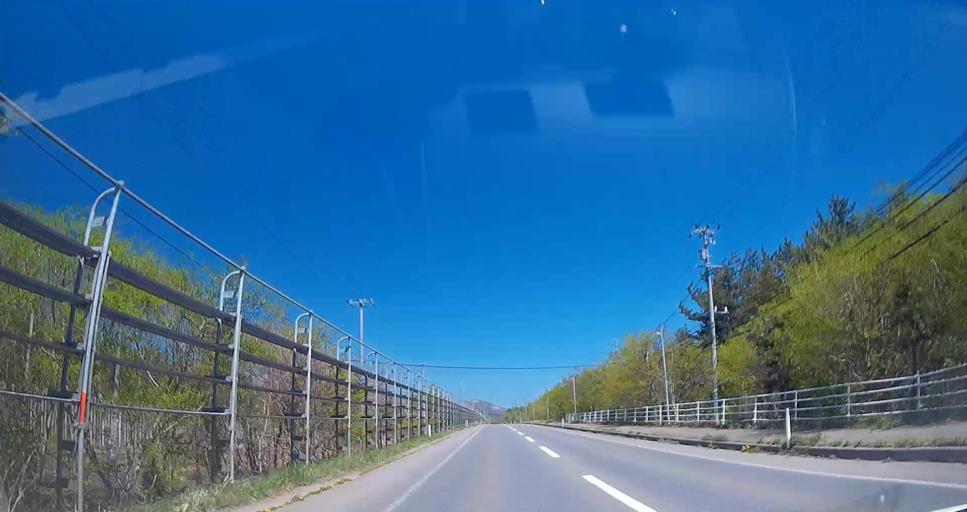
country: JP
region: Aomori
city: Misawa
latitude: 40.9733
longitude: 141.3597
